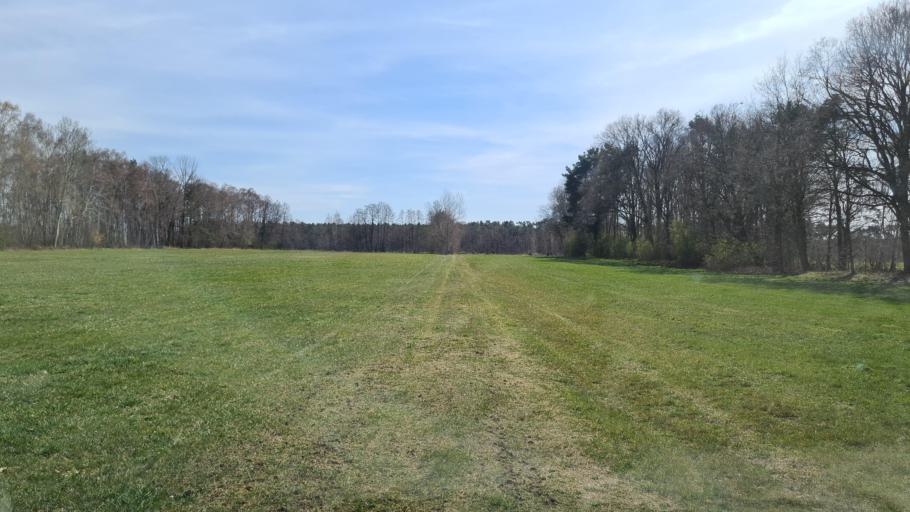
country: DE
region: Brandenburg
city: Finsterwalde
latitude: 51.6052
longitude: 13.6409
